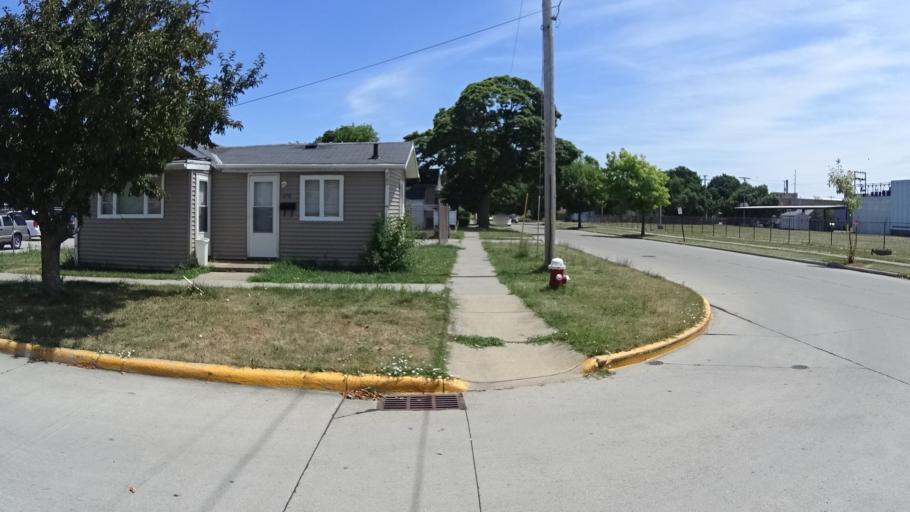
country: US
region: Ohio
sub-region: Erie County
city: Sandusky
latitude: 41.4391
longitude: -82.7156
